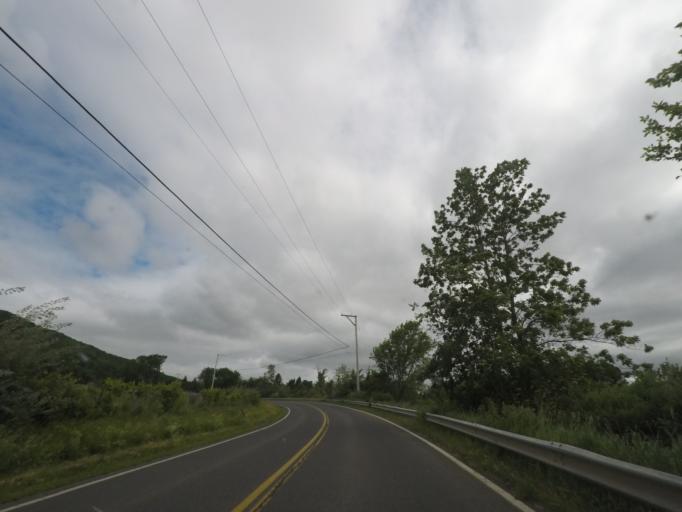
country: US
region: New York
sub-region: Dutchess County
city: Pine Plains
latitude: 41.9914
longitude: -73.5113
